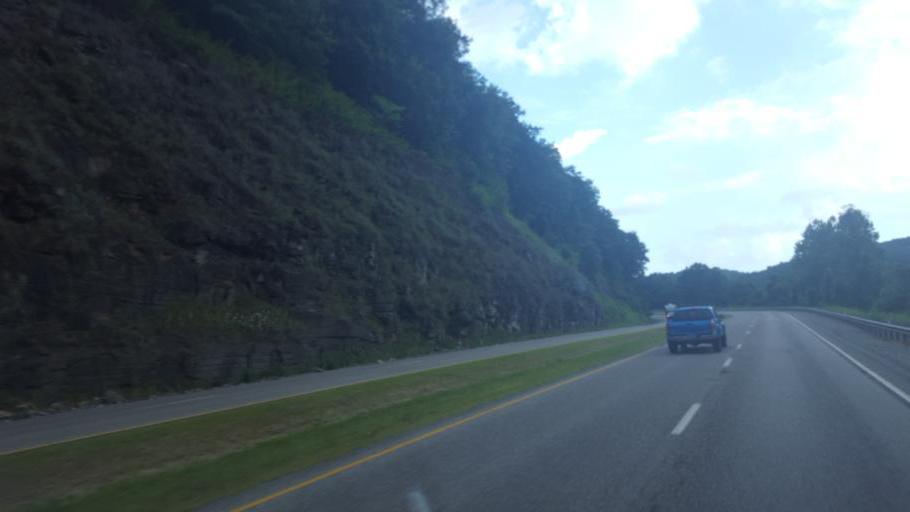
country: US
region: Virginia
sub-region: Wise County
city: Wise
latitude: 37.0316
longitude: -82.5976
